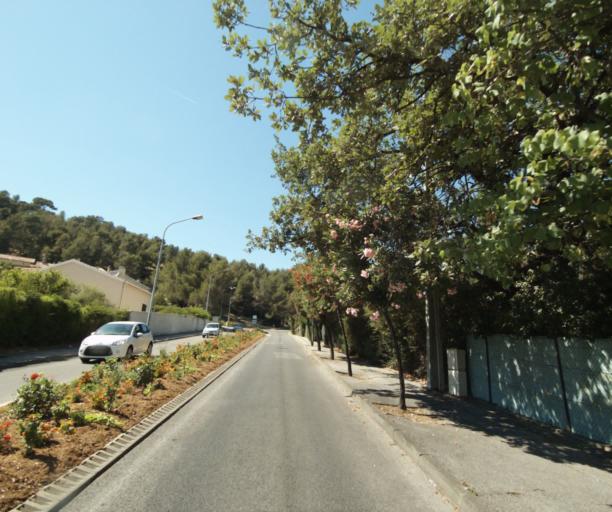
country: FR
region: Provence-Alpes-Cote d'Azur
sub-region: Departement du Var
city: La Garde
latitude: 43.1320
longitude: 6.0097
